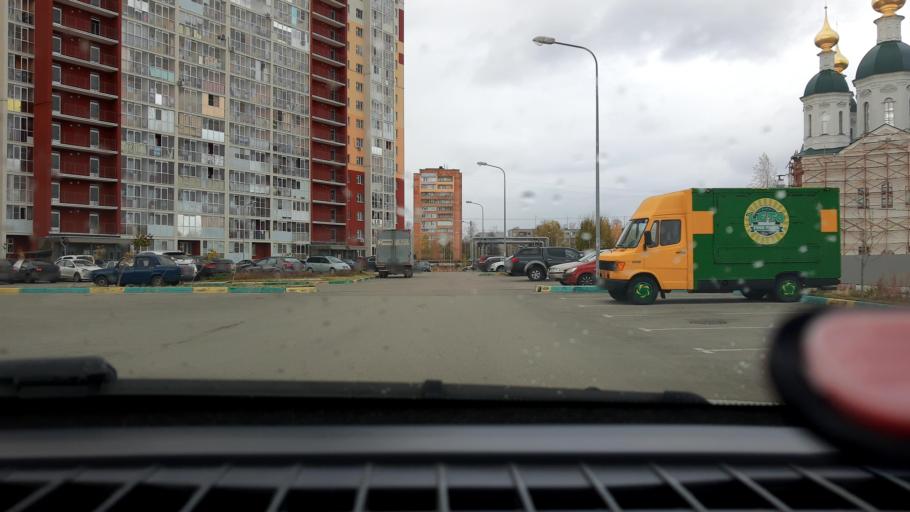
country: RU
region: Nizjnij Novgorod
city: Burevestnik
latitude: 56.2195
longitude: 43.8688
